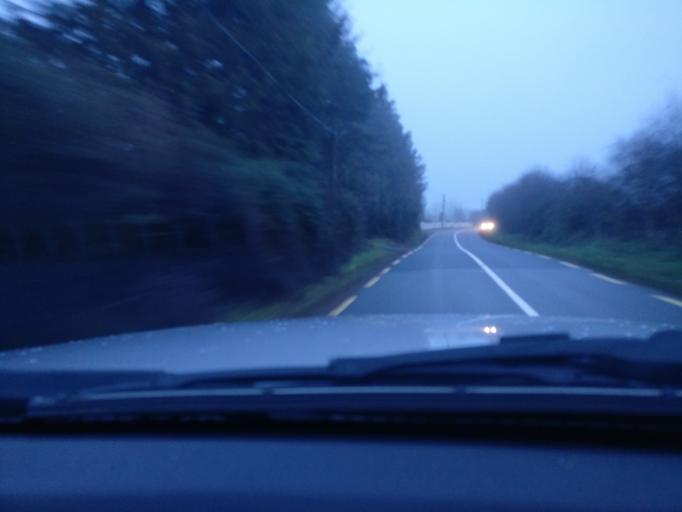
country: IE
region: Leinster
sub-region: An Mhi
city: Athboy
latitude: 53.6074
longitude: -6.9765
